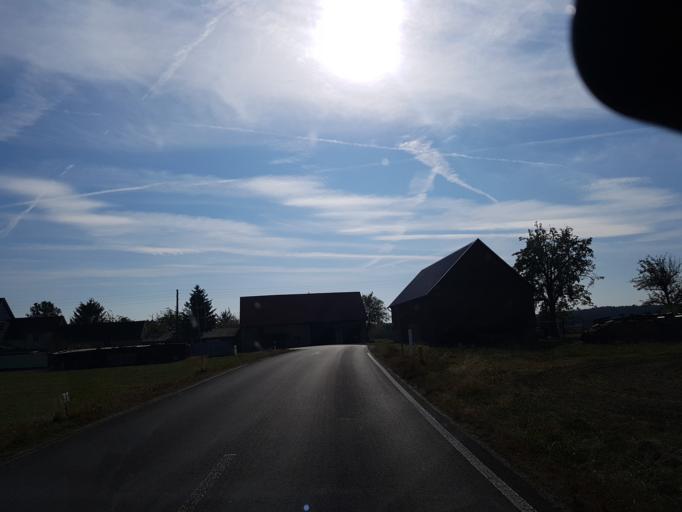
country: DE
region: Brandenburg
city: Schonborn
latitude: 51.6719
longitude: 13.4721
